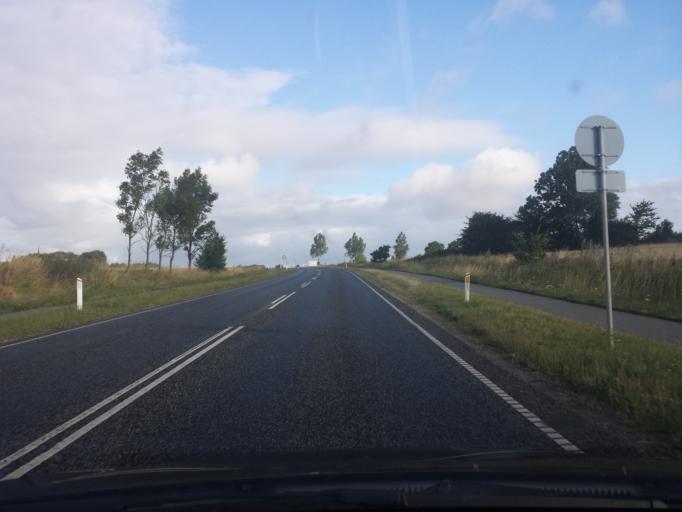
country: DK
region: South Denmark
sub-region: Sonderborg Kommune
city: Guderup
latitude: 54.9824
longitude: 9.8759
